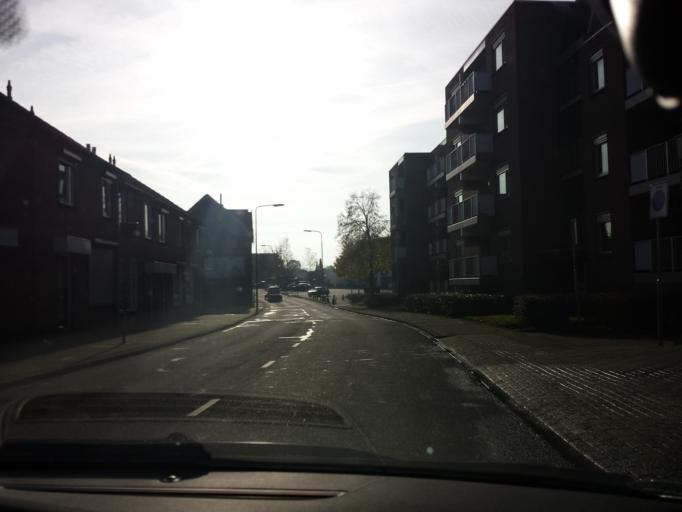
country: NL
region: Limburg
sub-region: Gemeente Kerkrade
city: Kerkrade
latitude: 50.8518
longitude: 6.0668
